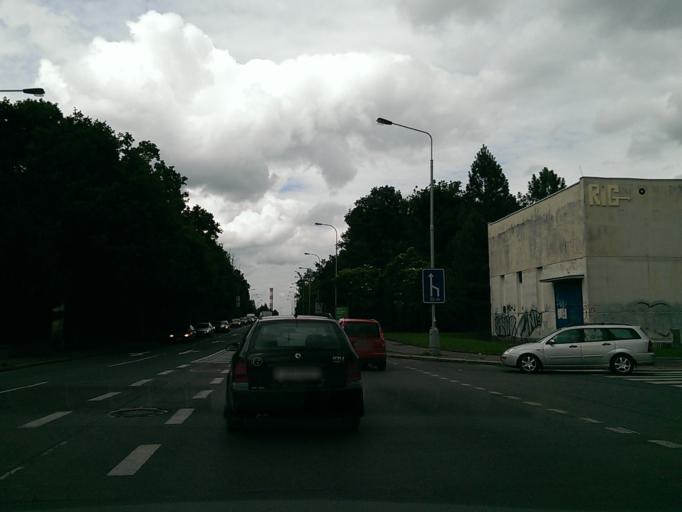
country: CZ
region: Praha
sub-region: Praha 4
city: Hodkovicky
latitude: 50.0245
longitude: 14.4424
